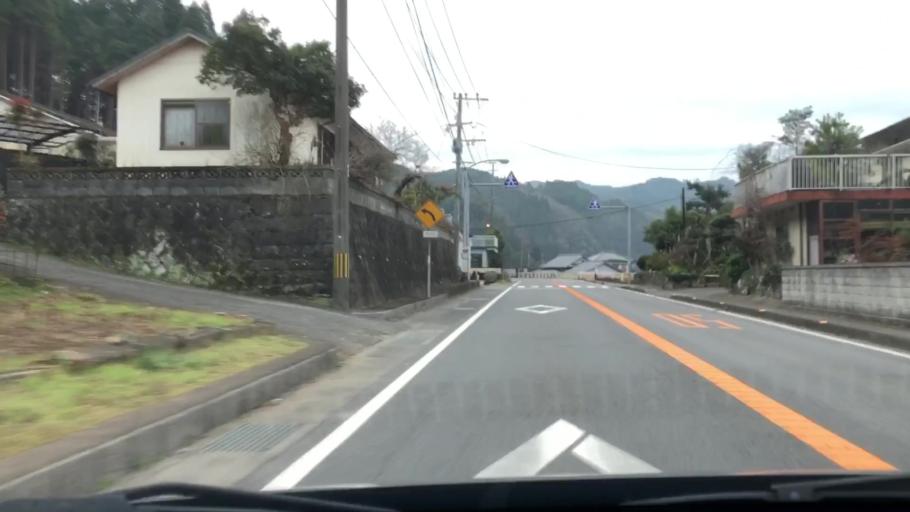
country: JP
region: Oita
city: Usuki
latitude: 33.0084
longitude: 131.7081
